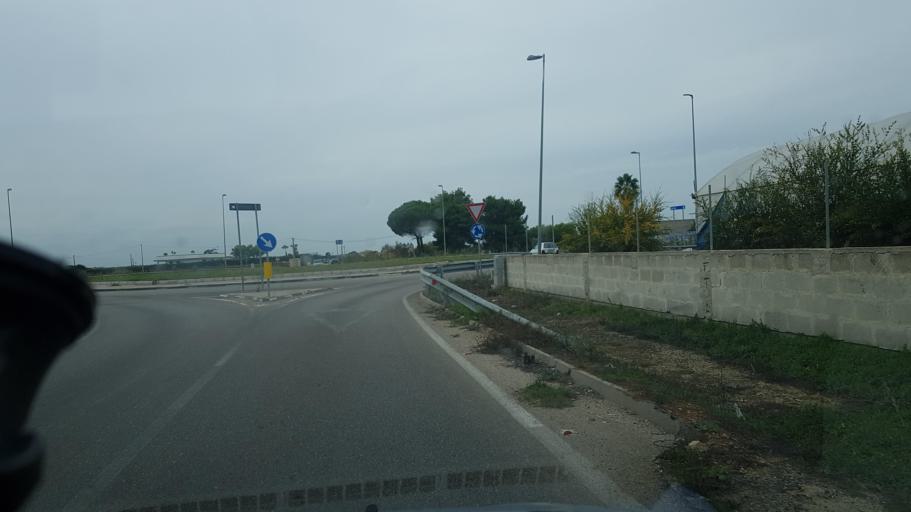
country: IT
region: Apulia
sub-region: Provincia di Lecce
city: Leverano
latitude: 40.3053
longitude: 17.9903
